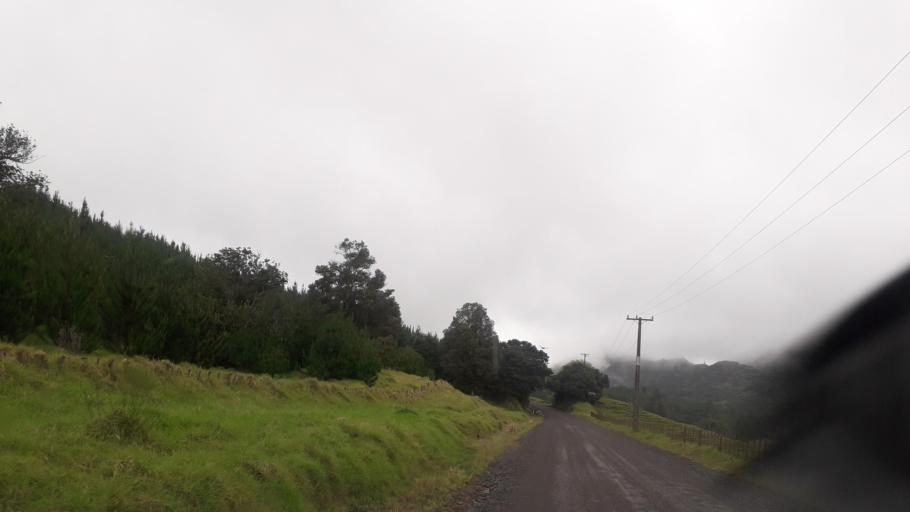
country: NZ
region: Northland
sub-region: Far North District
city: Ahipara
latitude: -35.4345
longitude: 173.3397
